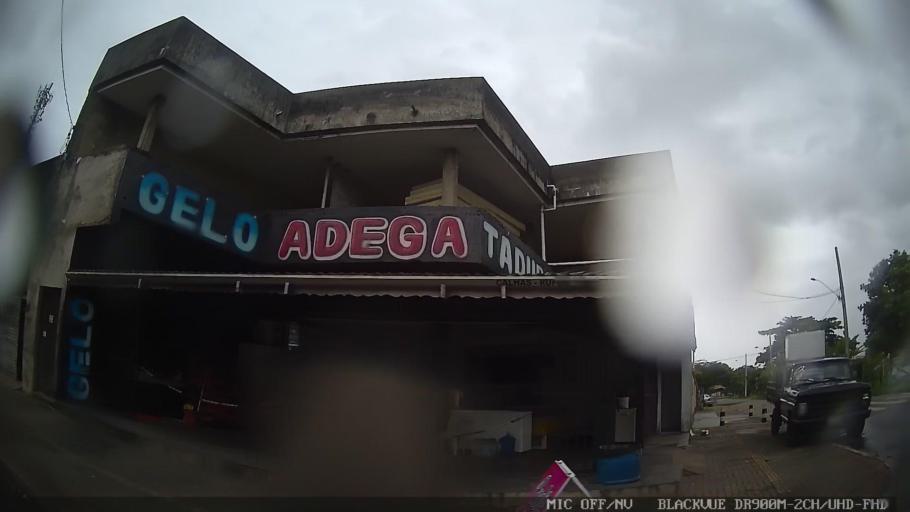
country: BR
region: Sao Paulo
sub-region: Mongagua
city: Mongagua
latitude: -24.1294
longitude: -46.6881
